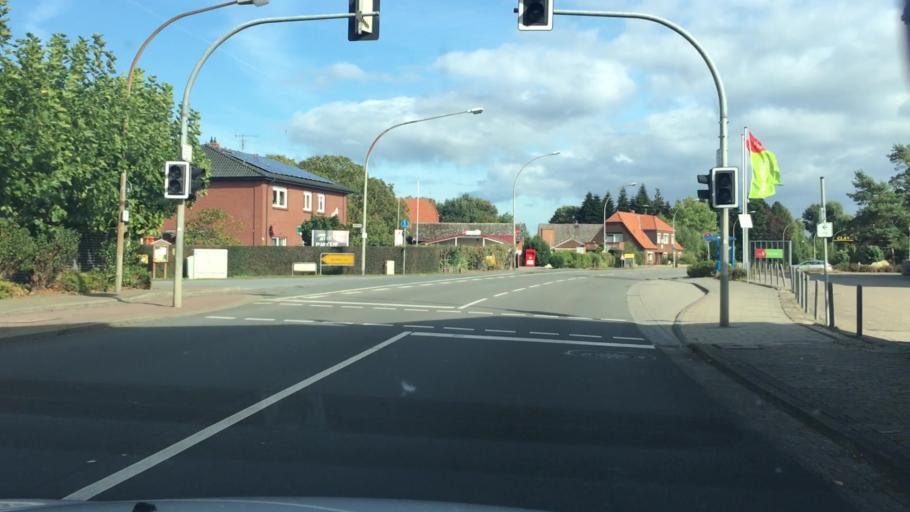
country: DE
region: Lower Saxony
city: Wetschen
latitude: 52.6138
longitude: 8.4523
